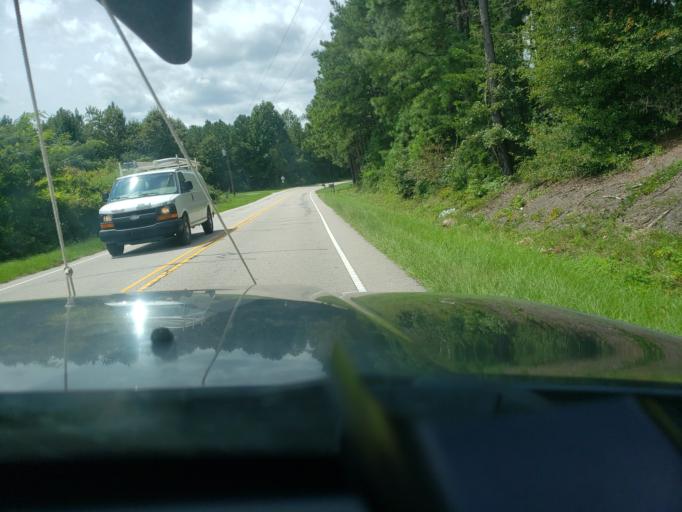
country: US
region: North Carolina
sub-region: Wake County
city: Rolesville
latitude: 35.8777
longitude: -78.4622
